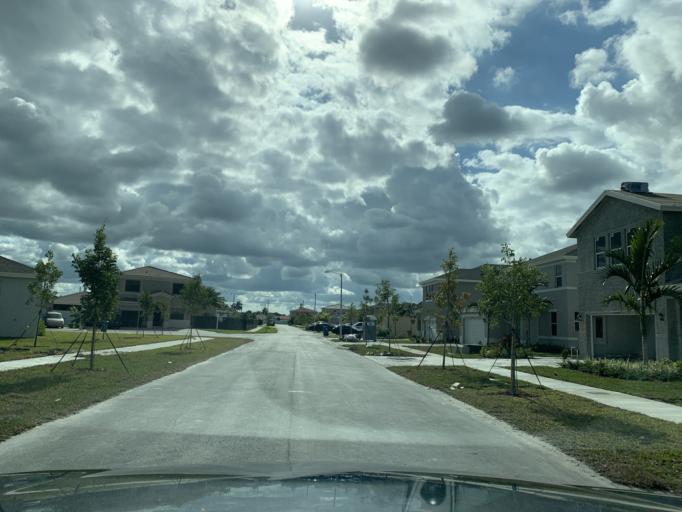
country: US
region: Florida
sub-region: Miami-Dade County
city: Naranja
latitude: 25.5113
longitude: -80.4097
